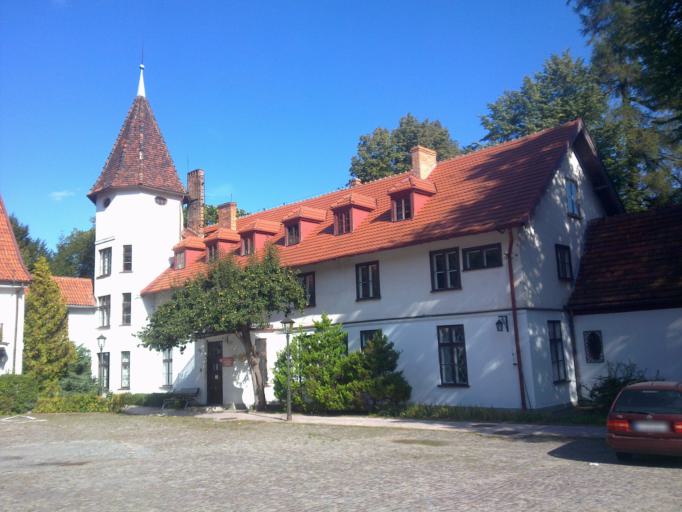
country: PL
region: Pomeranian Voivodeship
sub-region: Sopot
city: Sopot
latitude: 54.4196
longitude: 18.5592
